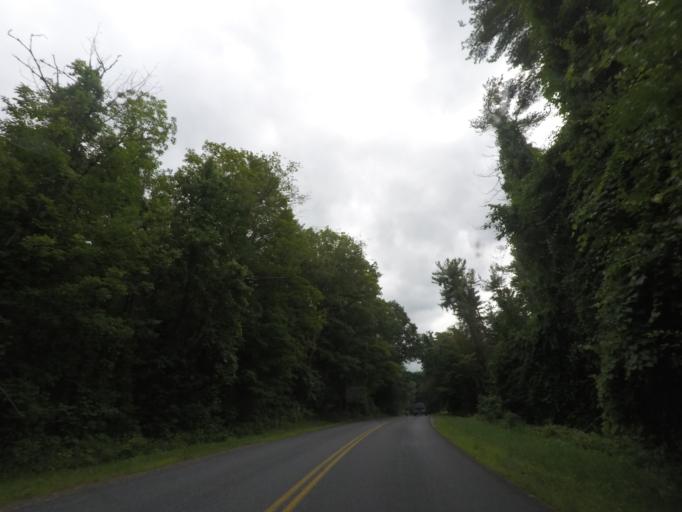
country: US
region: New York
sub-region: Saratoga County
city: Stillwater
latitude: 42.8543
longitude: -73.5455
